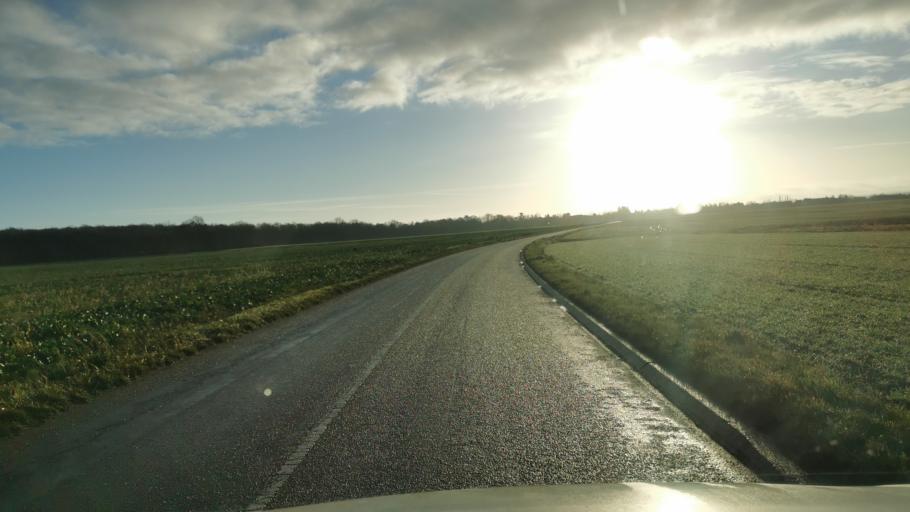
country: FR
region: Ile-de-France
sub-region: Departement des Yvelines
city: Houdan
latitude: 48.8317
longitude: 1.6240
